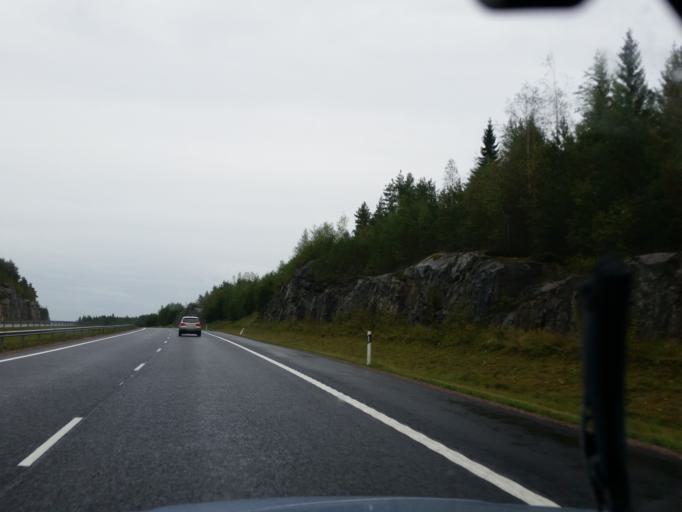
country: FI
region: Varsinais-Suomi
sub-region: Turku
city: Paimio
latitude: 60.4230
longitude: 22.7761
